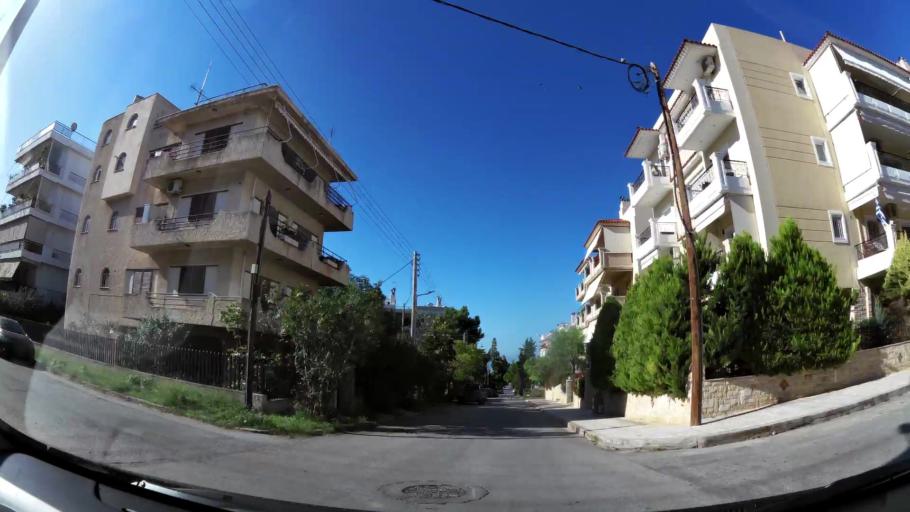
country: GR
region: Attica
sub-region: Nomarchia Athinas
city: Glyfada
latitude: 37.8703
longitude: 23.7679
